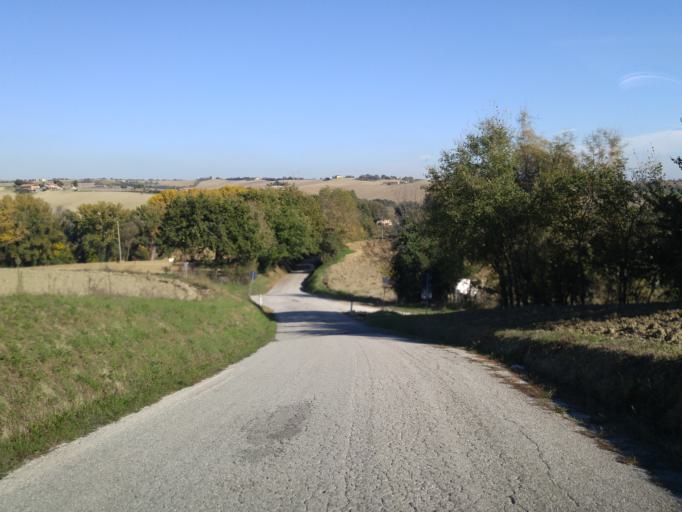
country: IT
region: The Marches
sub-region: Provincia di Pesaro e Urbino
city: Cartoceto
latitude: 43.7846
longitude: 12.8909
